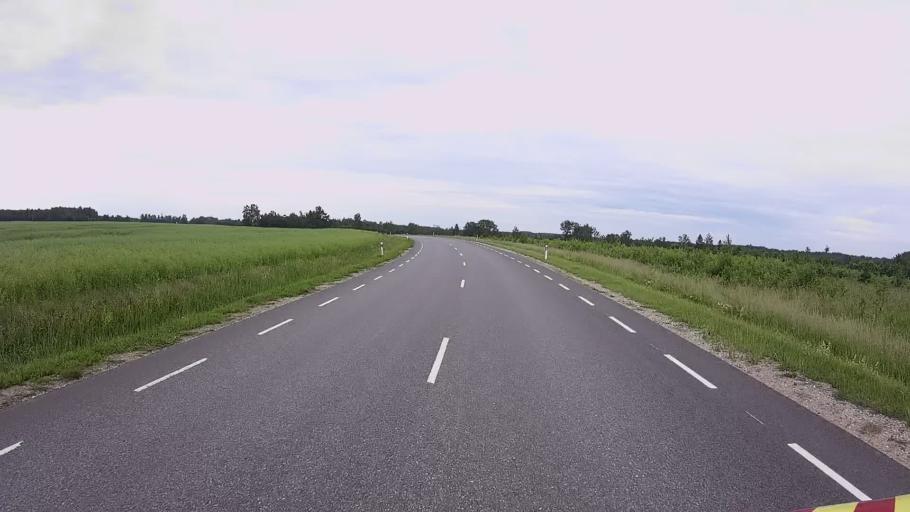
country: EE
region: Viljandimaa
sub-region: Karksi vald
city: Karksi-Nuia
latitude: 58.1708
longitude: 25.5802
